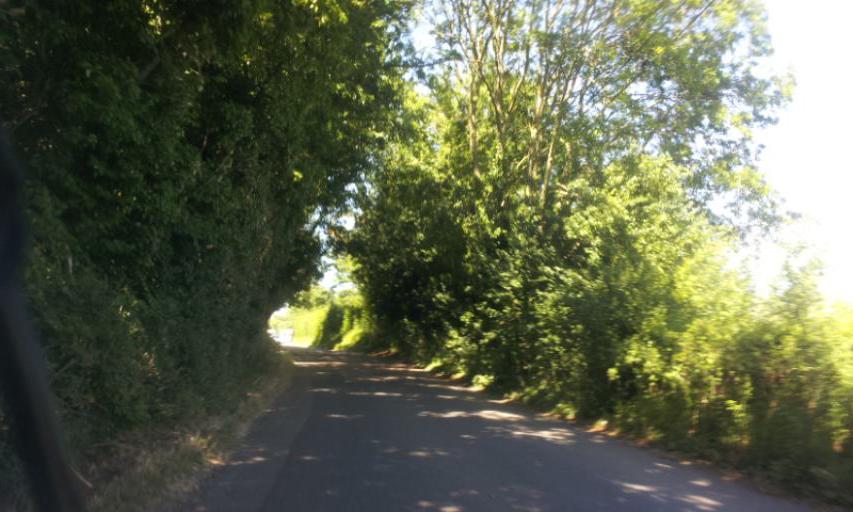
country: GB
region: England
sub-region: Kent
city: Teynham
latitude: 51.3411
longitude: 0.7754
